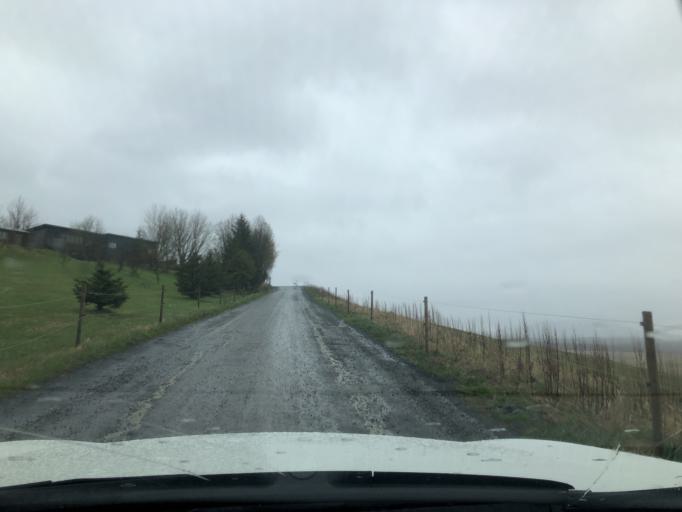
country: IS
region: South
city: Selfoss
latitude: 64.2409
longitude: -20.5489
